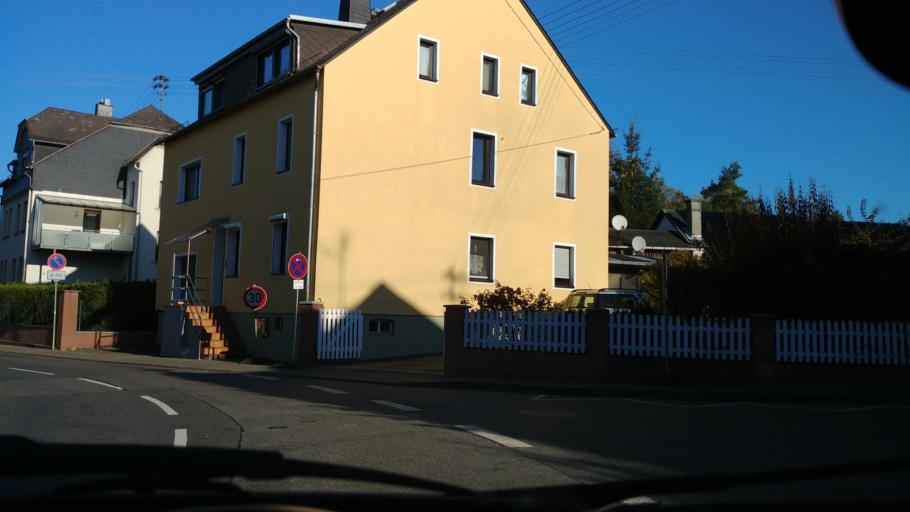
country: DE
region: Rheinland-Pfalz
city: Miehlen
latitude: 50.2245
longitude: 7.8332
